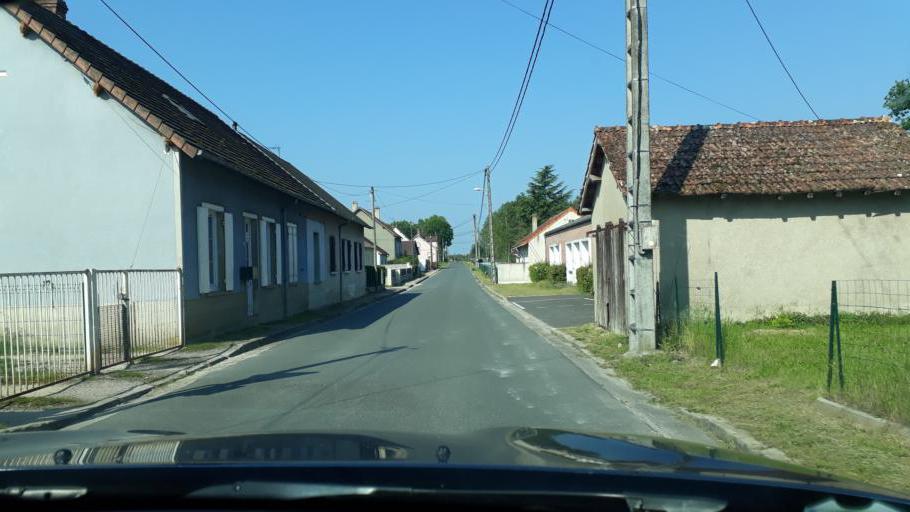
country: FR
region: Centre
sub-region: Departement du Loiret
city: Ligny-le-Ribault
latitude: 47.6226
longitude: 1.7520
